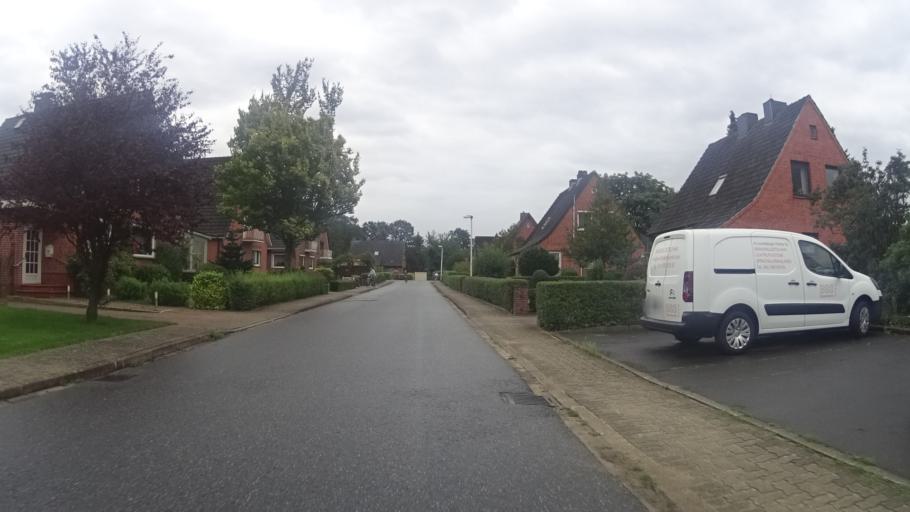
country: DE
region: Schleswig-Holstein
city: Kiebitzreihe
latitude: 53.7826
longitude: 9.6213
